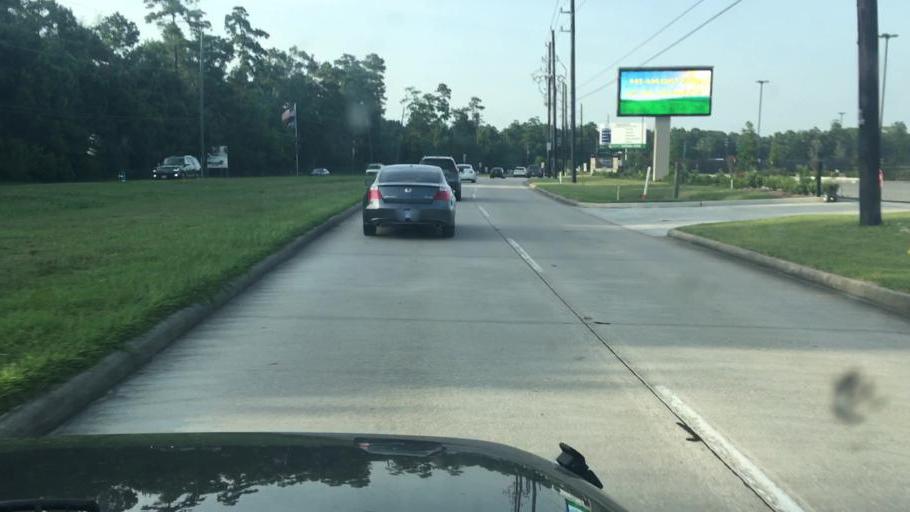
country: US
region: Texas
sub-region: Harris County
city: Atascocita
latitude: 29.9747
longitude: -95.1714
